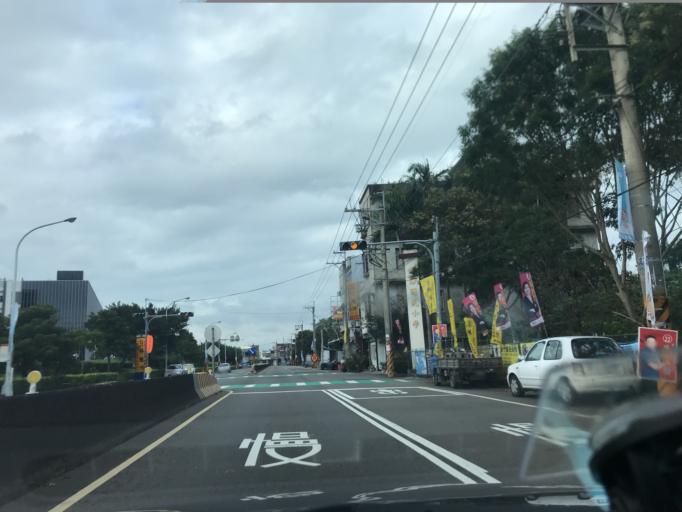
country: TW
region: Taiwan
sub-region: Hsinchu
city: Zhubei
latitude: 24.8049
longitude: 121.0495
